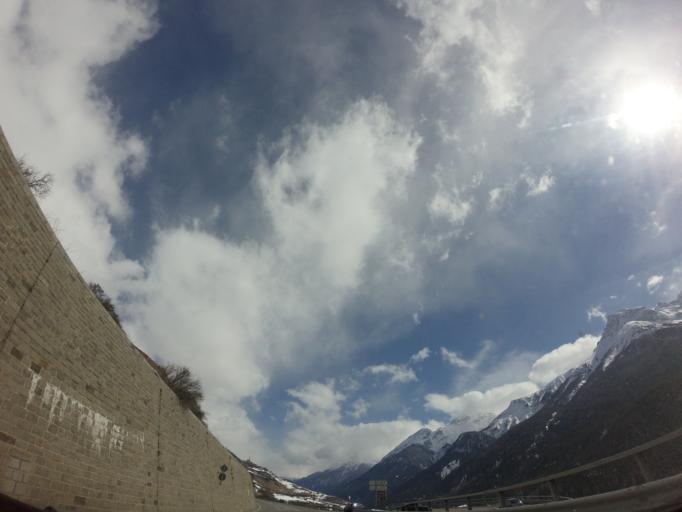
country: CH
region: Grisons
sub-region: Inn District
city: Scuol
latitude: 46.8014
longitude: 10.3106
